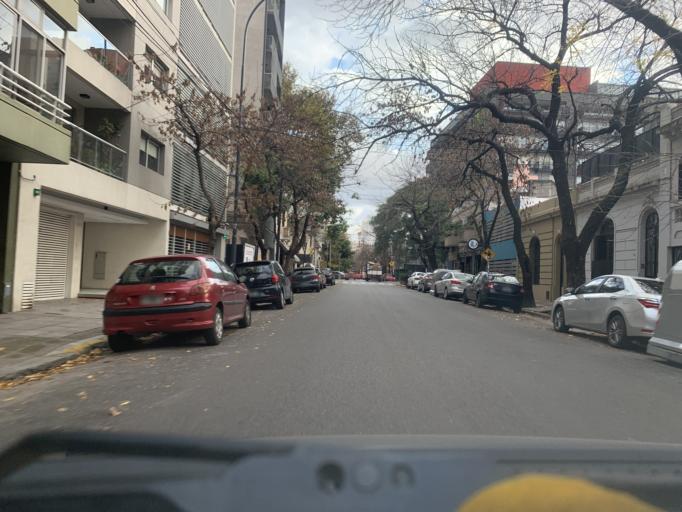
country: AR
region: Buenos Aires F.D.
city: Colegiales
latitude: -34.5770
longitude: -58.4380
